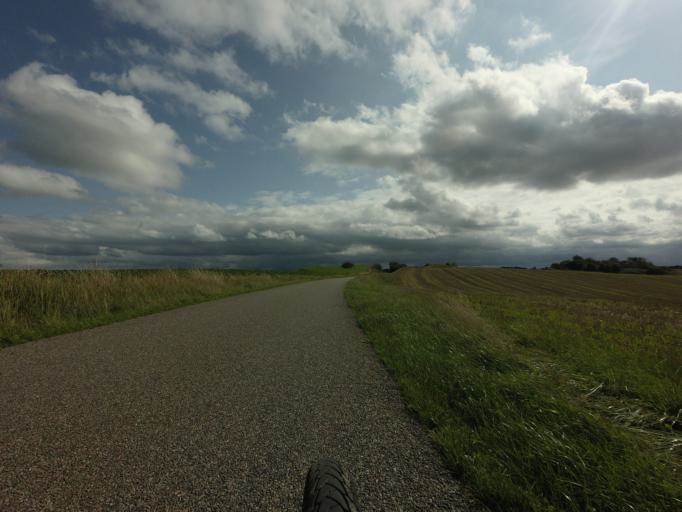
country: DK
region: North Denmark
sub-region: Hjorring Kommune
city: Hjorring
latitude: 57.5288
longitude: 10.0442
